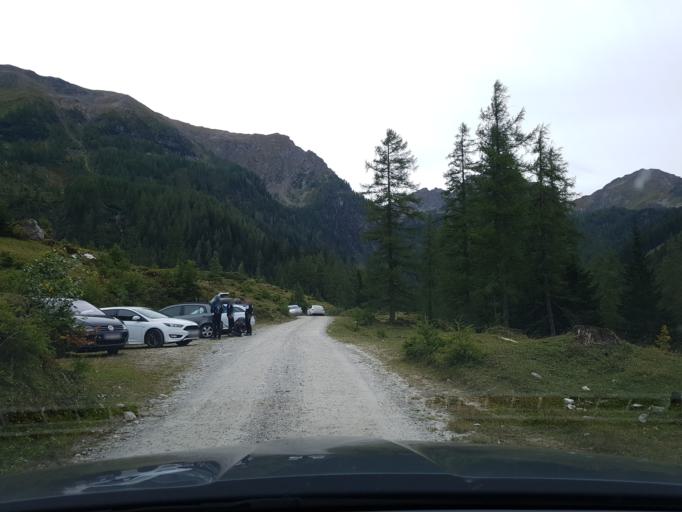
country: AT
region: Salzburg
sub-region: Politischer Bezirk Sankt Johann im Pongau
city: Untertauern
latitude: 47.2940
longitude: 13.5803
